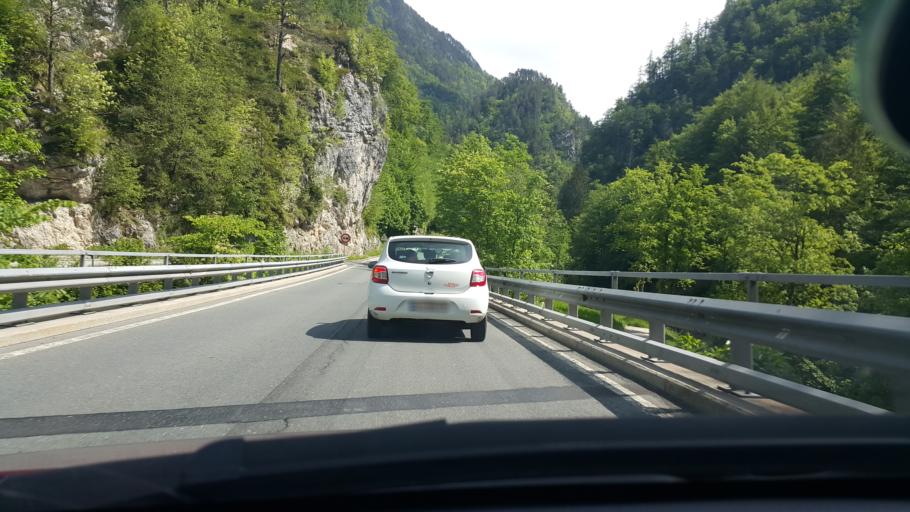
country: AT
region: Carinthia
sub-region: Politischer Bezirk Klagenfurt Land
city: Ferlach
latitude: 46.4809
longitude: 14.2590
